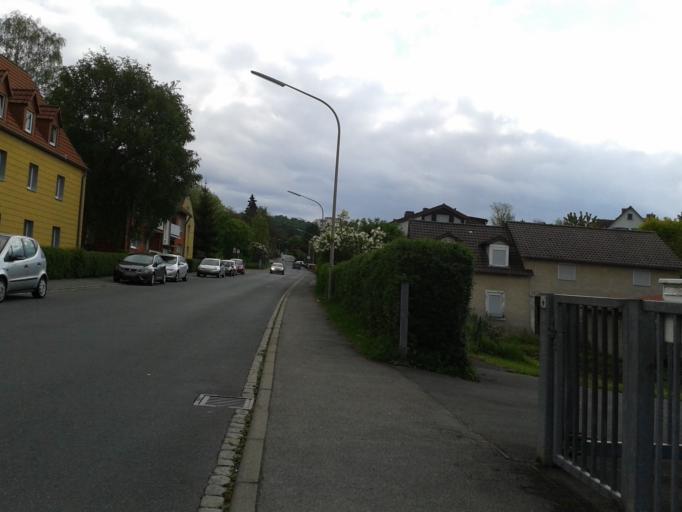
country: DE
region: Bavaria
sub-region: Upper Franconia
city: Kronach
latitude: 50.2404
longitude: 11.3359
